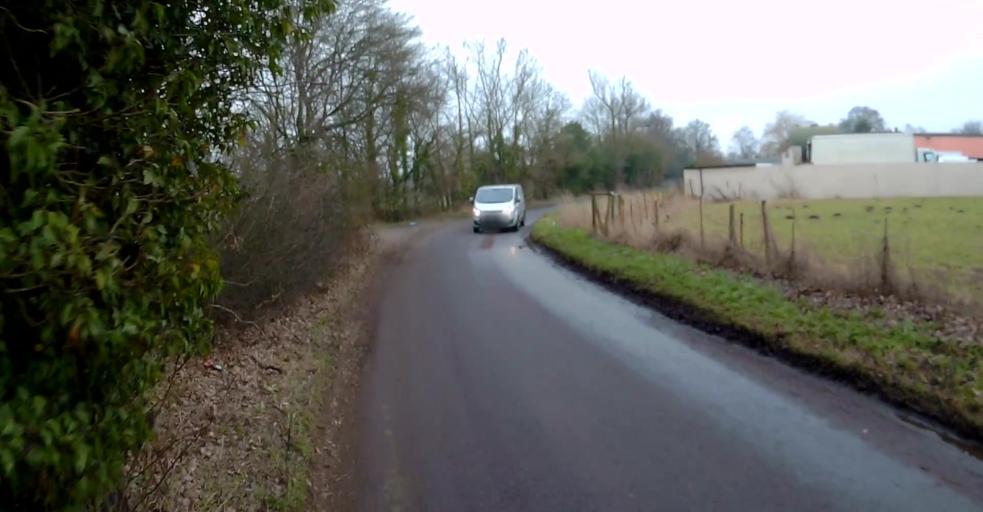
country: GB
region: England
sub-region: Hampshire
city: Eversley
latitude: 51.3670
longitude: -0.8890
